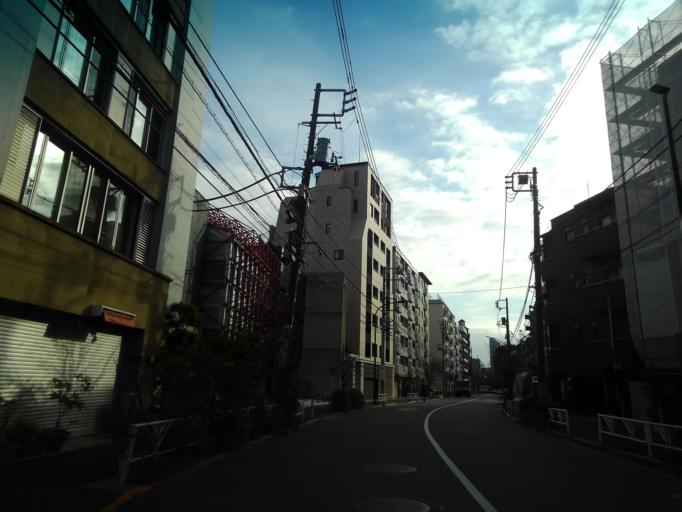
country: JP
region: Tokyo
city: Tokyo
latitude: 35.6639
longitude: 139.6804
